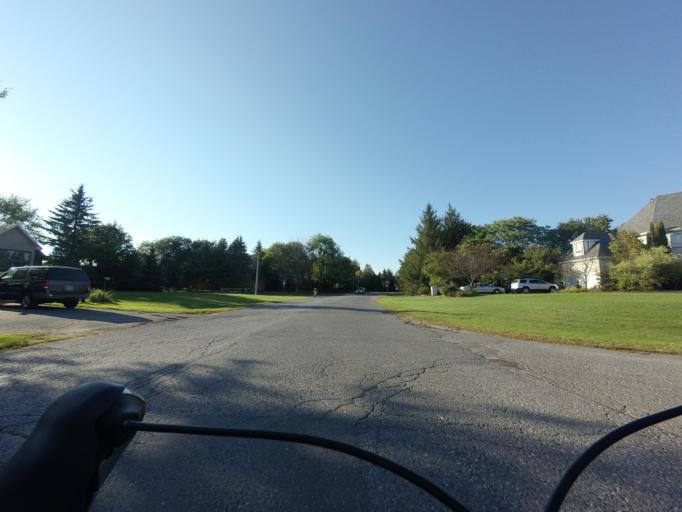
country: CA
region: Ontario
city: Bells Corners
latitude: 45.2198
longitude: -75.6978
